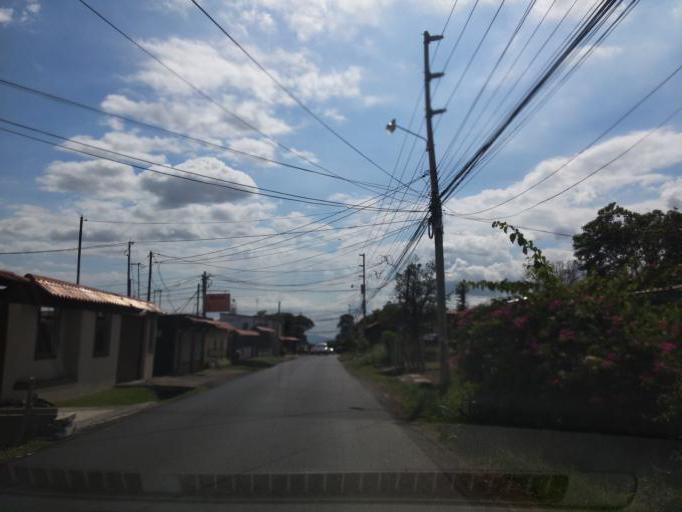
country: CR
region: Alajuela
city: Alajuela
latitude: 10.0192
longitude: -84.1818
